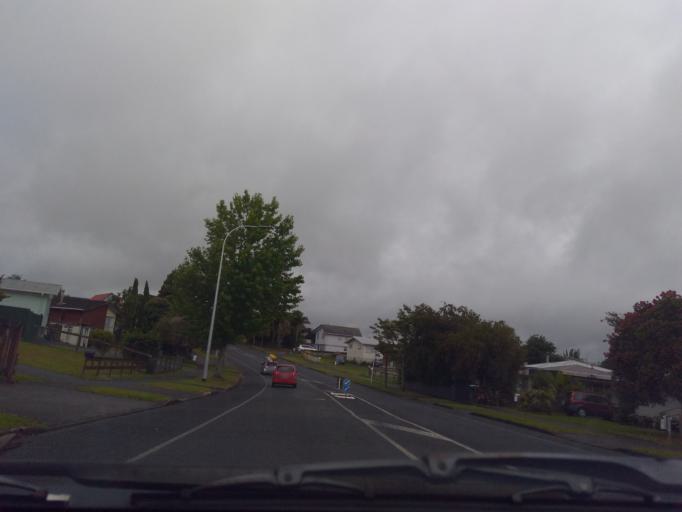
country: NZ
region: Northland
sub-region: Whangarei
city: Whangarei
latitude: -35.6850
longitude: 174.3256
